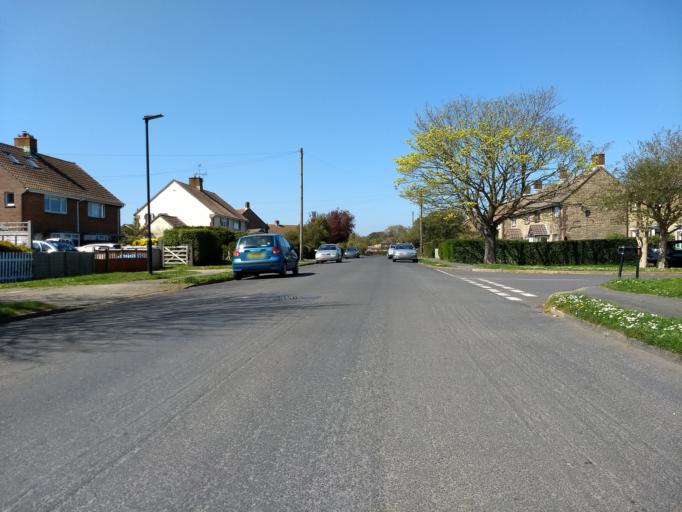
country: GB
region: England
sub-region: Isle of Wight
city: Bembridge
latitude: 50.6851
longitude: -1.0776
